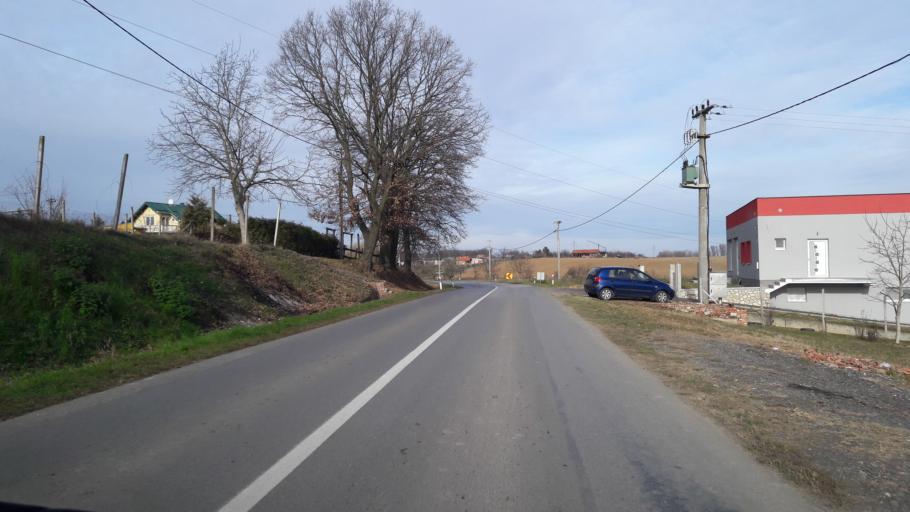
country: HR
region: Osjecko-Baranjska
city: Piskorevci
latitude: 45.2981
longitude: 18.4281
